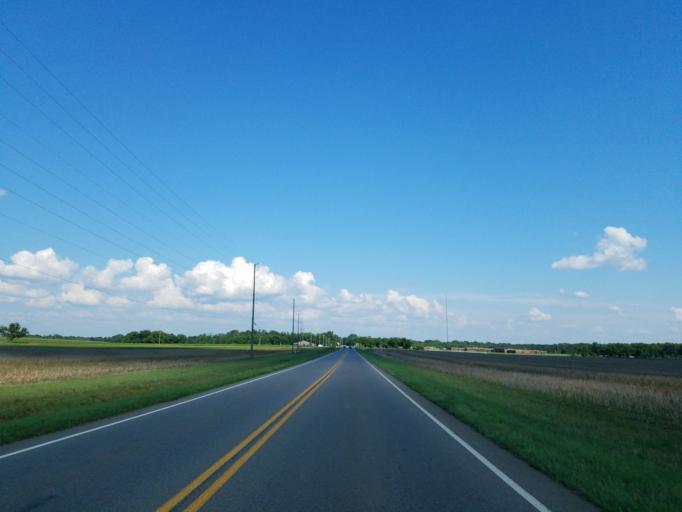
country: US
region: Georgia
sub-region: Peach County
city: Fort Valley
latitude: 32.5791
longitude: -83.9140
